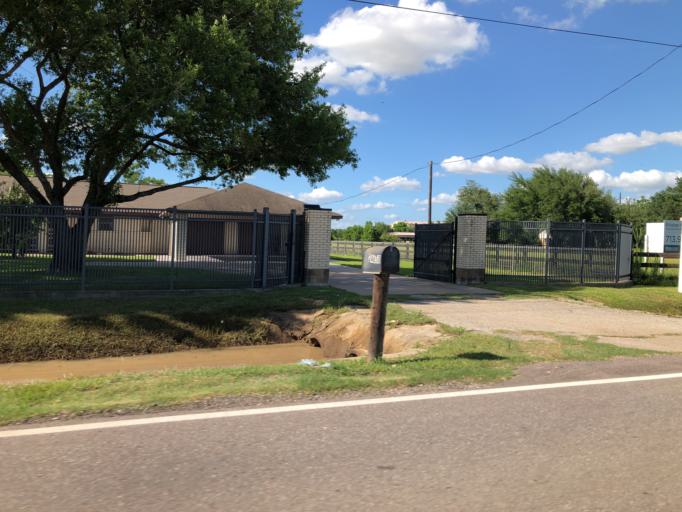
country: US
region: Texas
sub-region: Harris County
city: Katy
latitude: 29.8314
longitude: -95.8019
